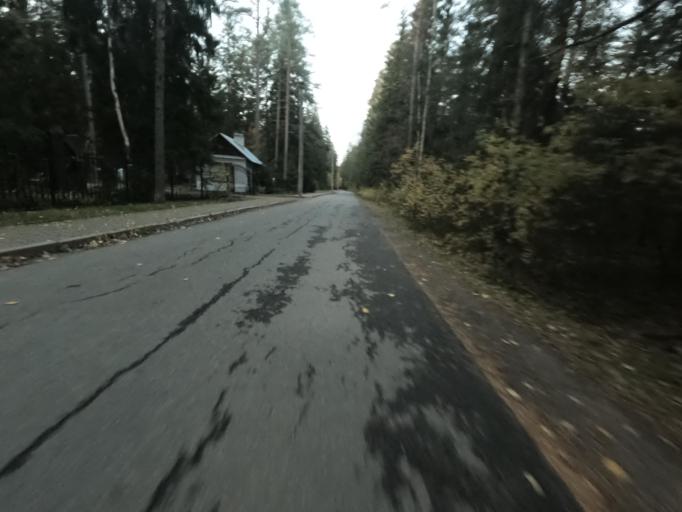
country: RU
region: St.-Petersburg
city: Komarovo
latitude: 60.2037
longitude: 29.8004
